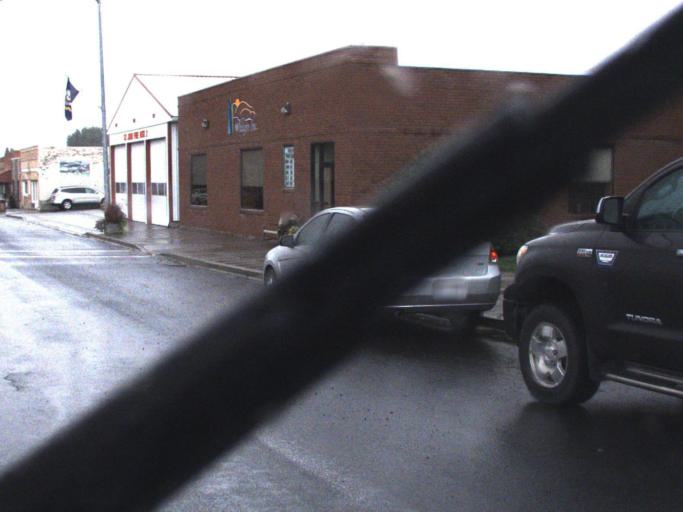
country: US
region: Washington
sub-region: Whitman County
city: Colfax
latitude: 47.0918
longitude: -117.5795
